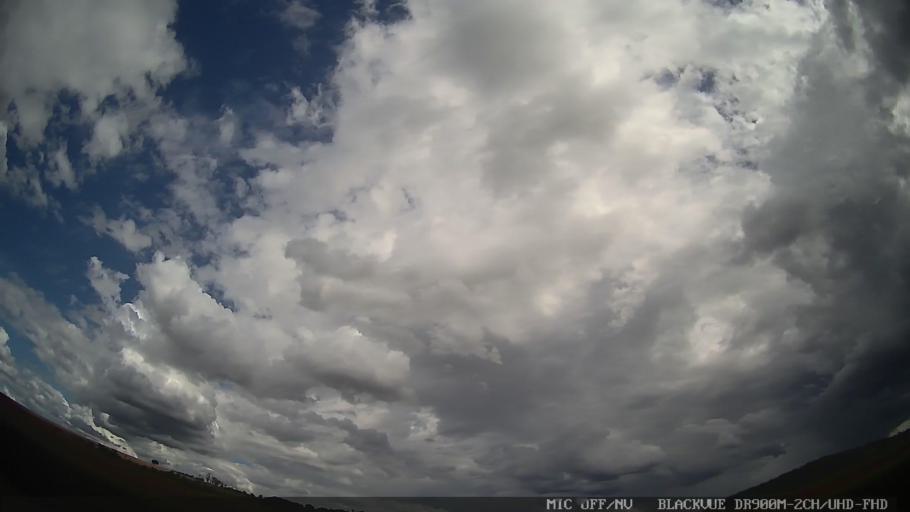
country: BR
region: Sao Paulo
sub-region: Jaguariuna
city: Jaguariuna
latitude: -22.6685
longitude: -46.9617
